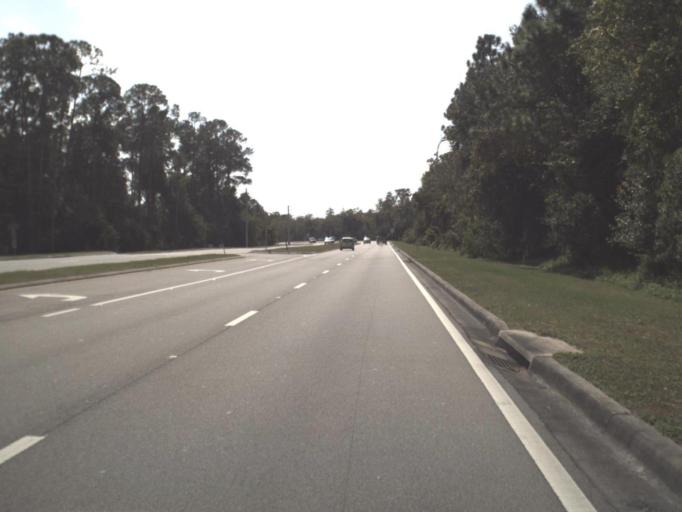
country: US
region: Florida
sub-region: Osceola County
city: Celebration
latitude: 28.3226
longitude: -81.4901
